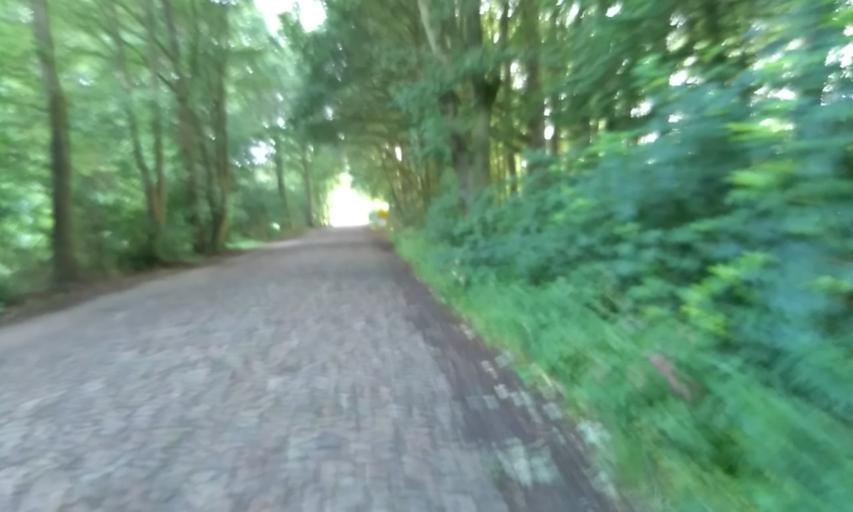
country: DE
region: Lower Saxony
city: Deinste
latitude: 53.5066
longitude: 9.4518
